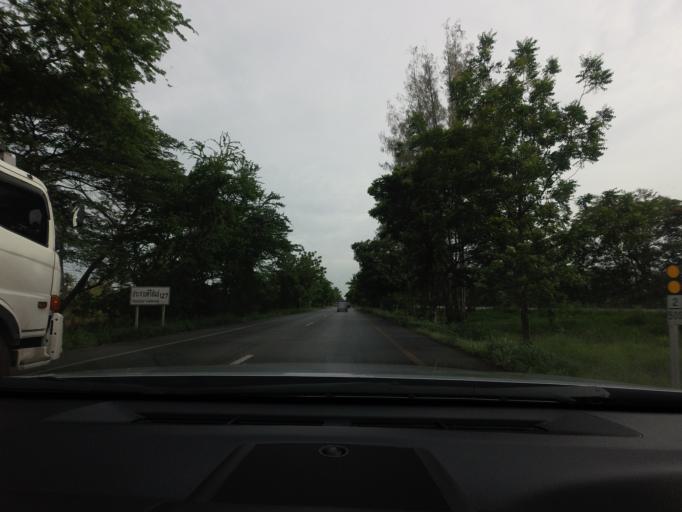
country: TH
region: Phetchaburi
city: Cha-am
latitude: 12.7882
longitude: 99.9393
